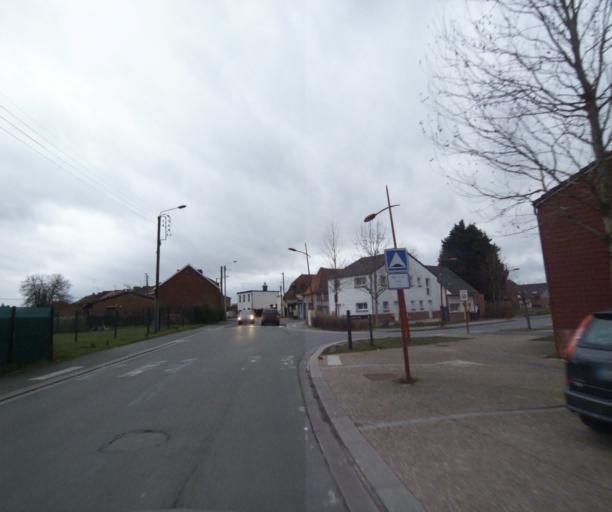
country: FR
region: Nord-Pas-de-Calais
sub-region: Departement du Nord
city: Anzin
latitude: 50.3843
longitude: 3.5151
